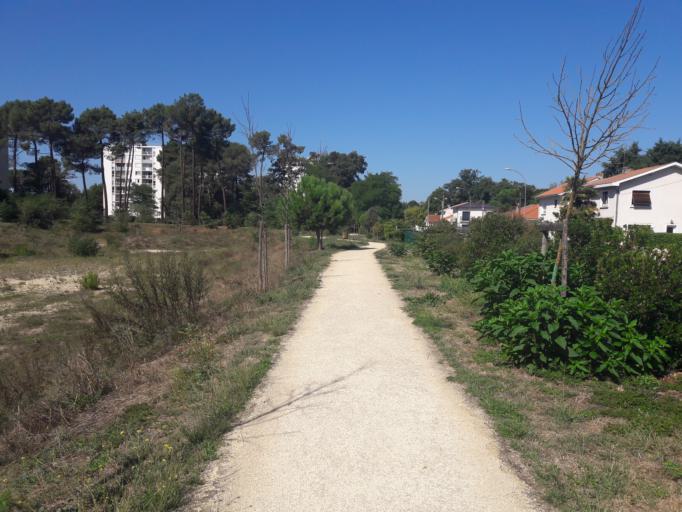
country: FR
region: Aquitaine
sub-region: Departement de la Gironde
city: Villenave-d'Ornon
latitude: 44.7614
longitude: -0.5744
